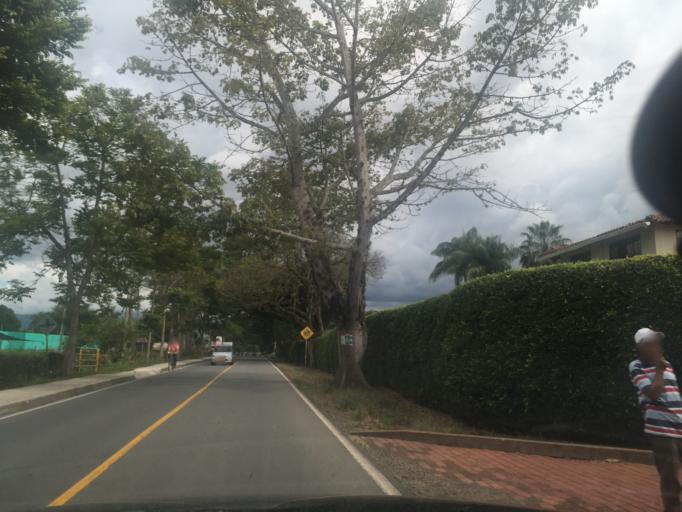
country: CO
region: Valle del Cauca
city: Caicedonia
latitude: 4.3420
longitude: -75.8490
